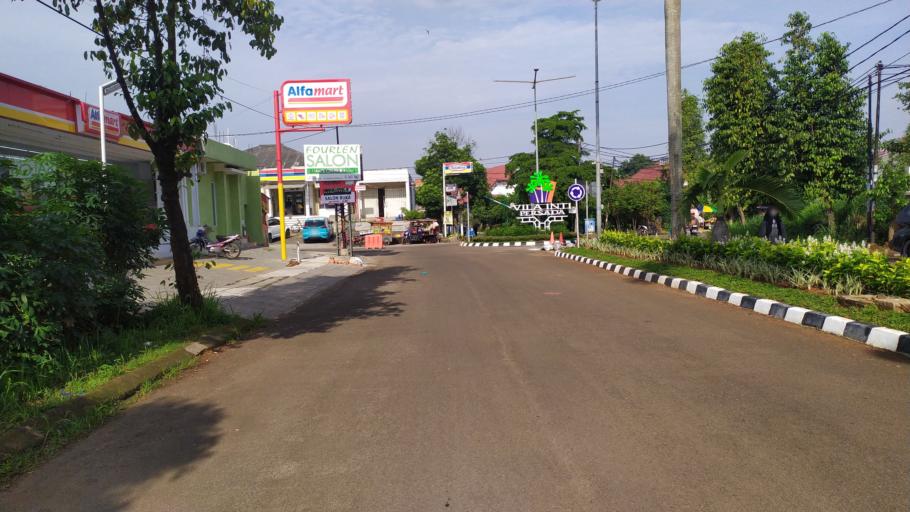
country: ID
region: West Java
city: Pamulang
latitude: -6.3570
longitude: 106.7462
